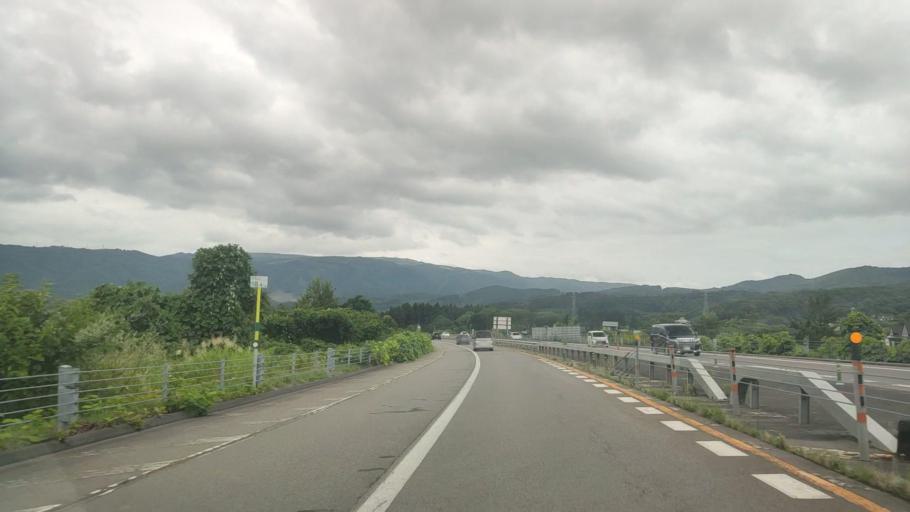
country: JP
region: Hokkaido
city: Nanae
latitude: 41.9199
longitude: 140.6802
